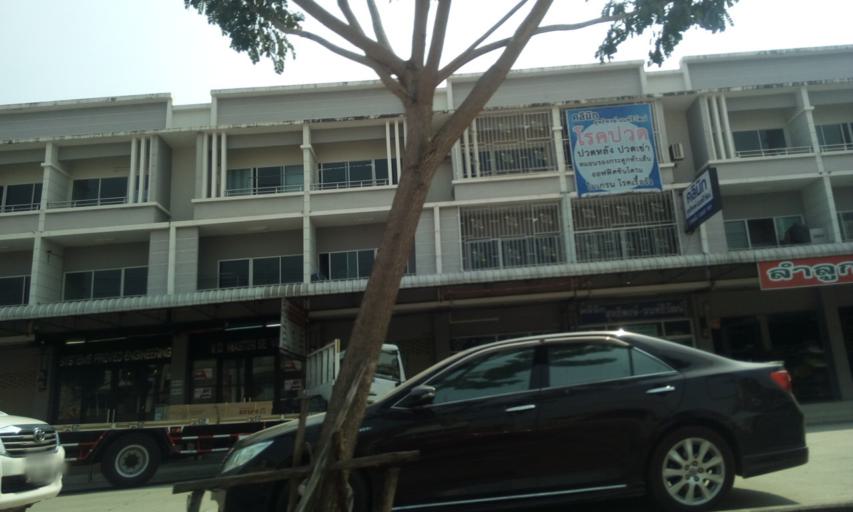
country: TH
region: Pathum Thani
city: Lam Luk Ka
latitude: 13.9645
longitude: 100.7414
